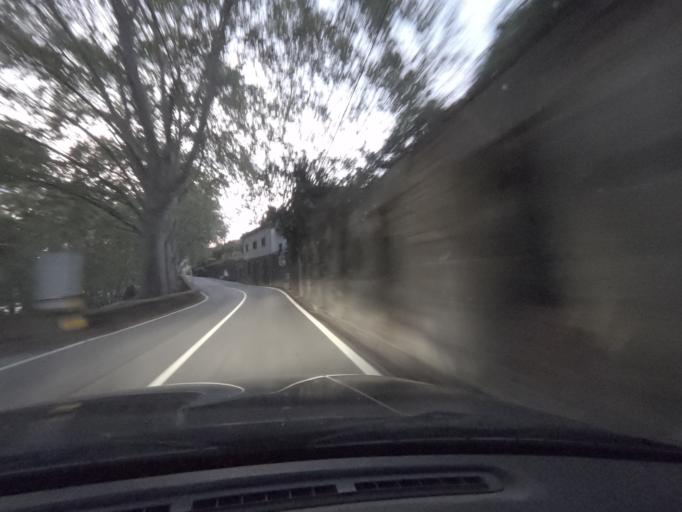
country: PT
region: Vila Real
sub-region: Peso da Regua
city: Godim
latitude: 41.1545
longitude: -7.8352
